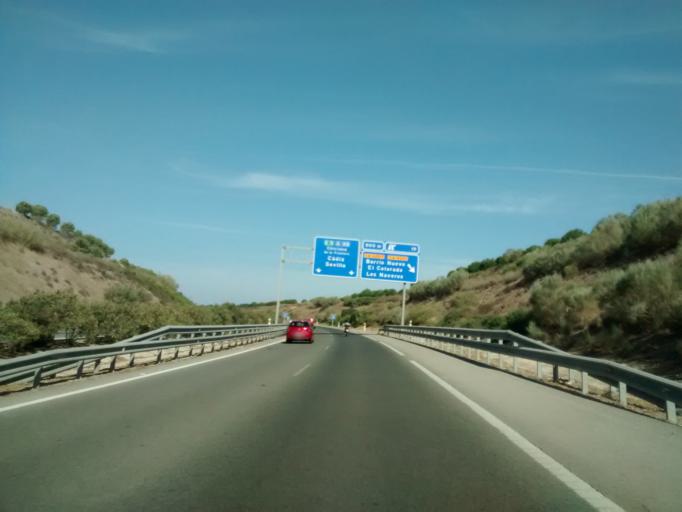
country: ES
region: Andalusia
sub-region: Provincia de Cadiz
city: Conil de la Frontera
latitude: 36.3432
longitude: -6.0517
